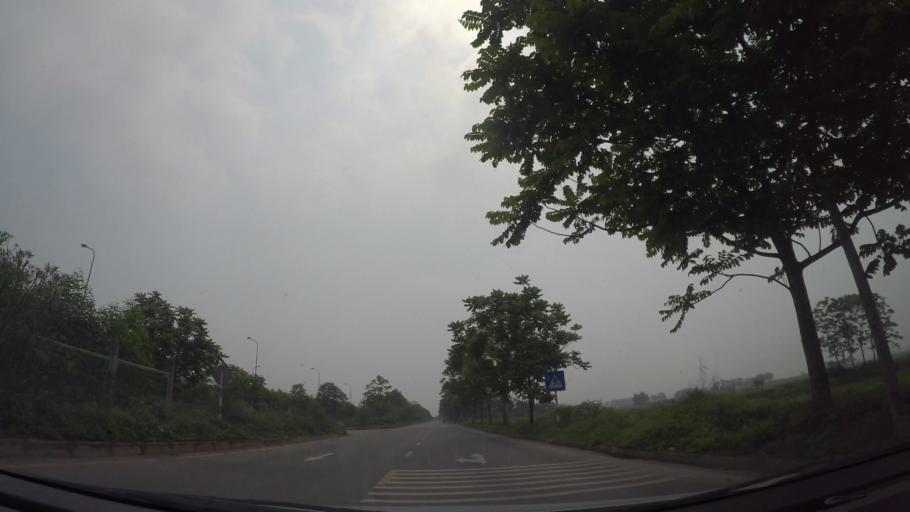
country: VN
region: Ha Noi
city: Lien Quan
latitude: 20.9889
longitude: 105.5662
